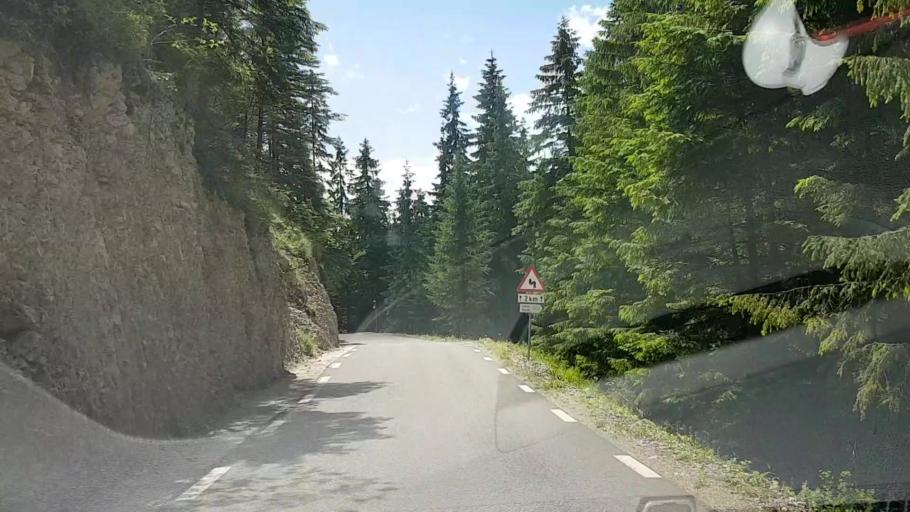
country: RO
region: Suceava
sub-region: Municipiul Campulung Moldovenesc
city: Campulung Moldovenesc
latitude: 47.4501
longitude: 25.5514
